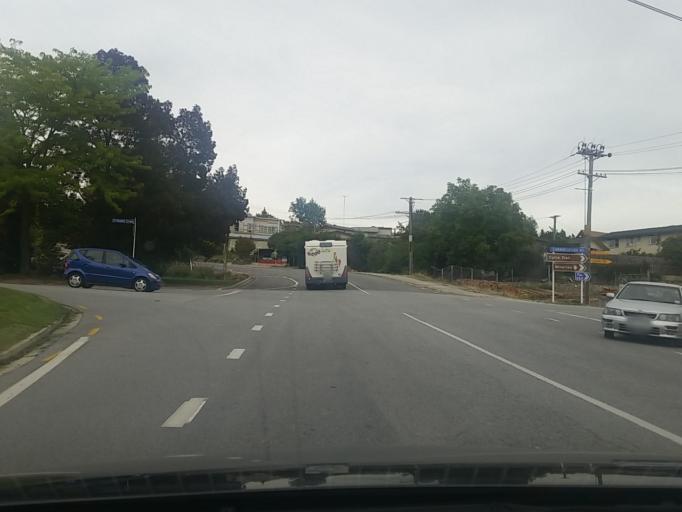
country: NZ
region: Otago
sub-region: Queenstown-Lakes District
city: Wanaka
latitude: -45.2607
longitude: 169.3884
